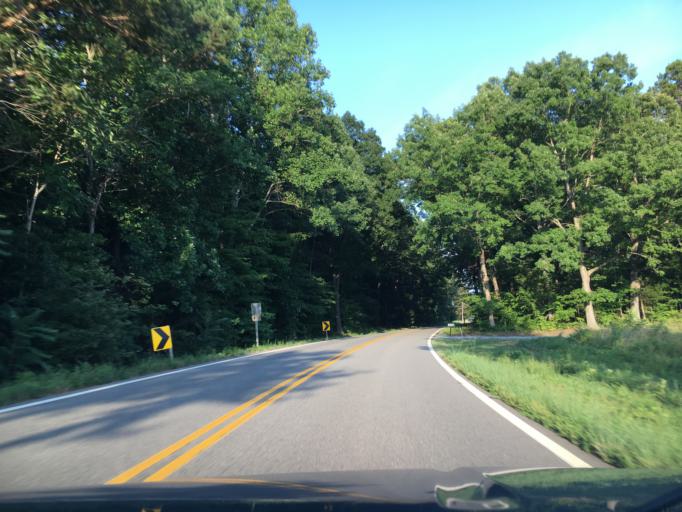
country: US
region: Virginia
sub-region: Halifax County
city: Mountain Road
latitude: 36.8354
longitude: -79.1296
